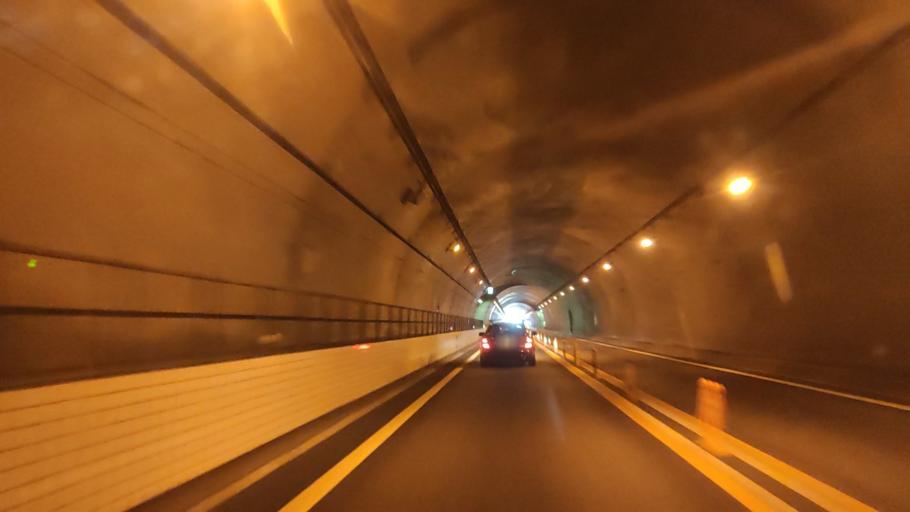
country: JP
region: Tokushima
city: Ikedacho
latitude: 34.0231
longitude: 133.7936
